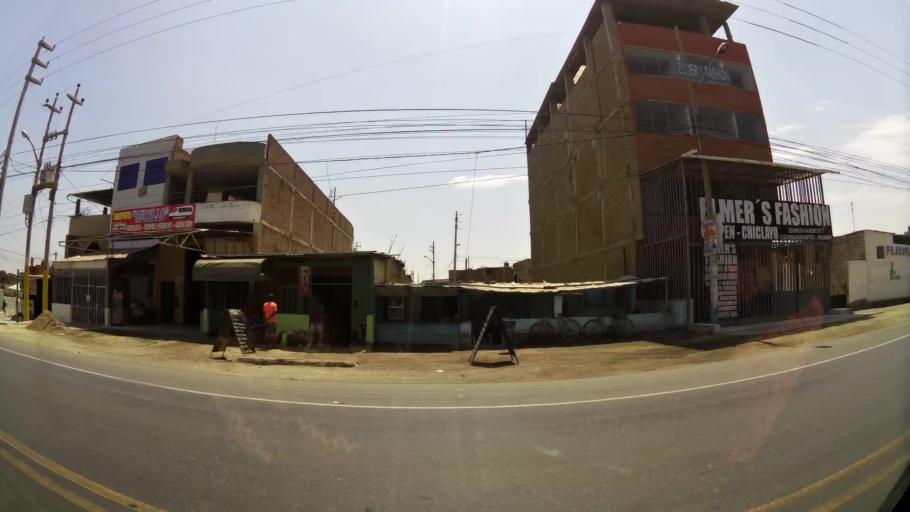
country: PE
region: La Libertad
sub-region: Chepen
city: Chepen
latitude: -7.2205
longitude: -79.4353
